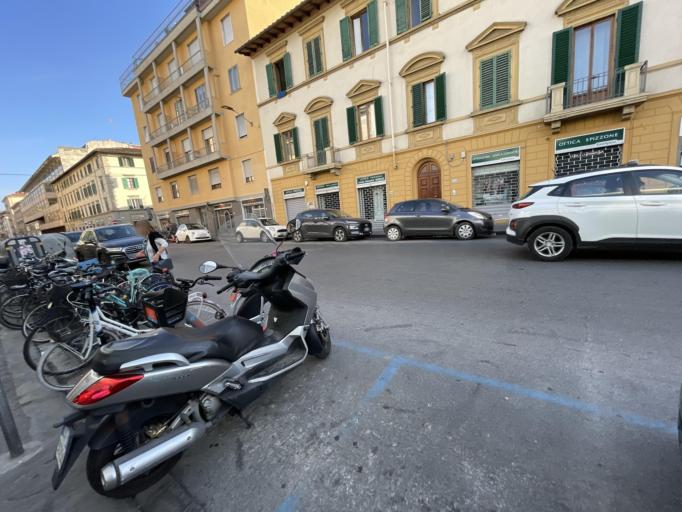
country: IT
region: Tuscany
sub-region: Province of Florence
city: Florence
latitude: 43.7848
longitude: 11.2668
